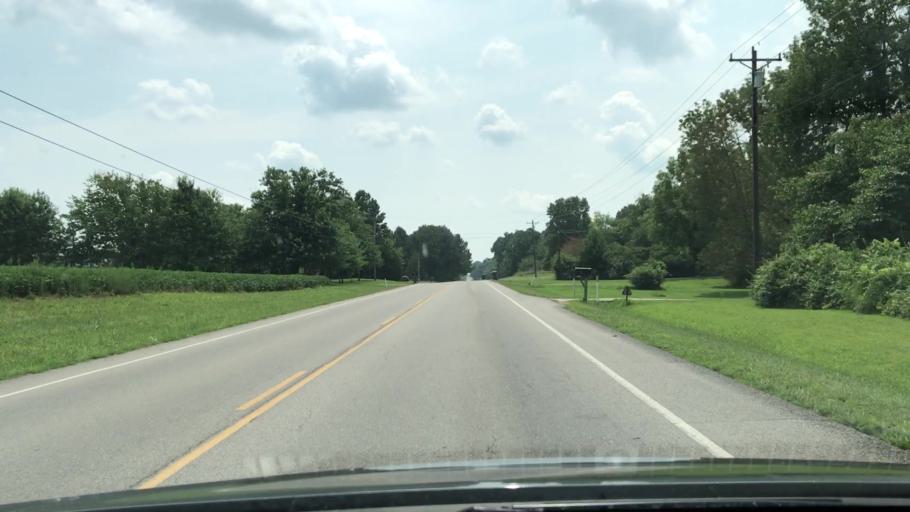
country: US
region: Tennessee
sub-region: Sumner County
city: Portland
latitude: 36.5310
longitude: -86.5031
